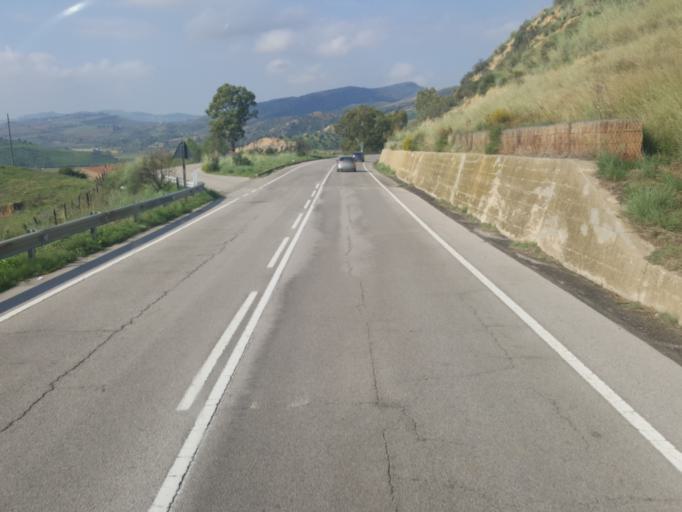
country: IT
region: Sicily
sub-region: Enna
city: Villarosa
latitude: 37.5082
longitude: 14.1848
